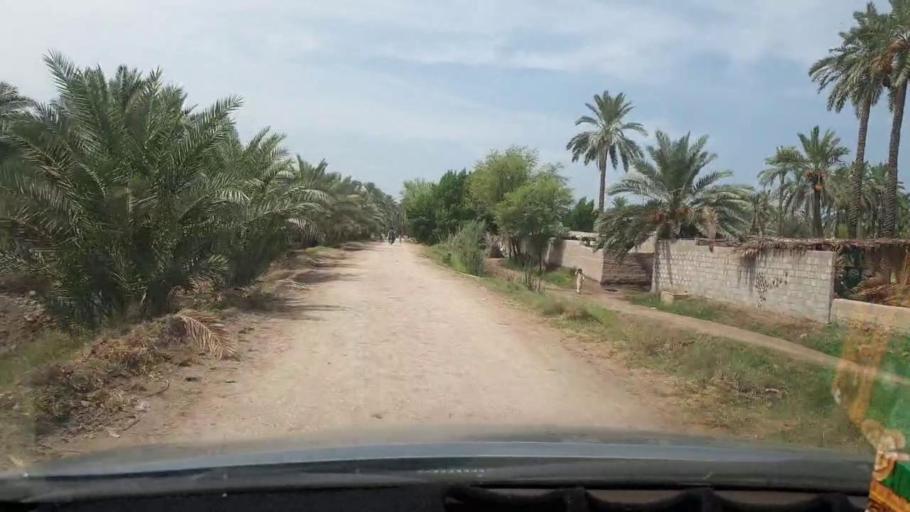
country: PK
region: Sindh
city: Khairpur
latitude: 27.4896
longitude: 68.7538
